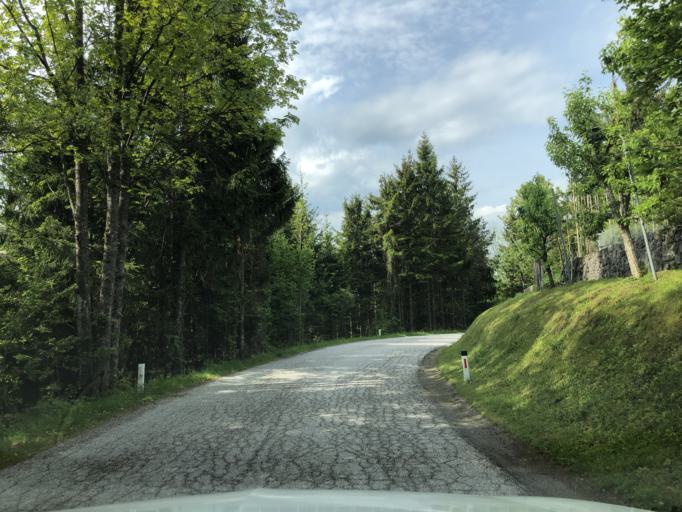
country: SI
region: Bloke
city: Nova Vas
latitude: 45.8015
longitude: 14.5499
